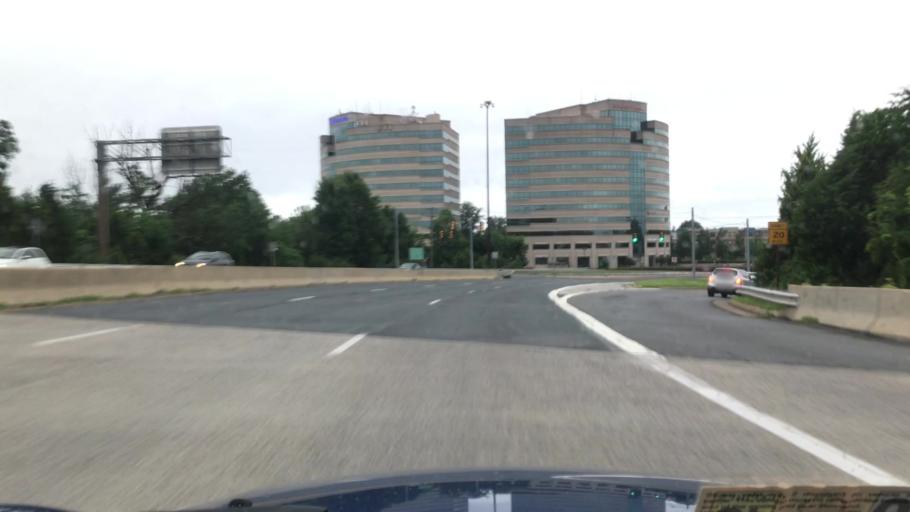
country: US
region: Virginia
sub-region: Fairfax County
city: Greenbriar
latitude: 38.8683
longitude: -77.3648
